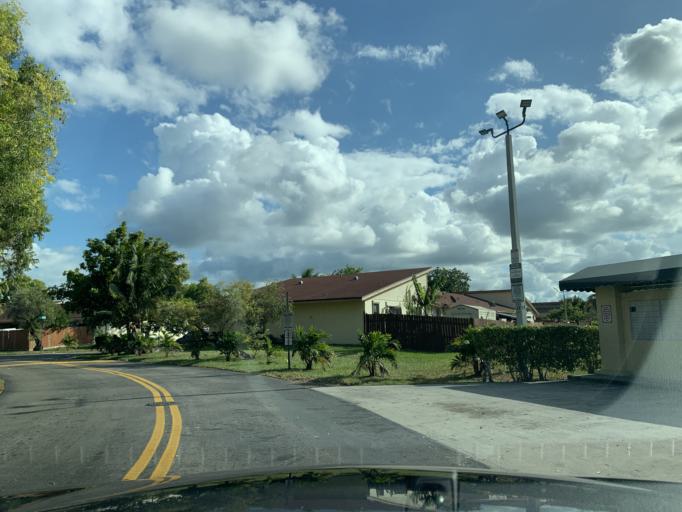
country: US
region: Florida
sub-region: Miami-Dade County
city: Naranja
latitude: 25.5063
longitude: -80.4198
